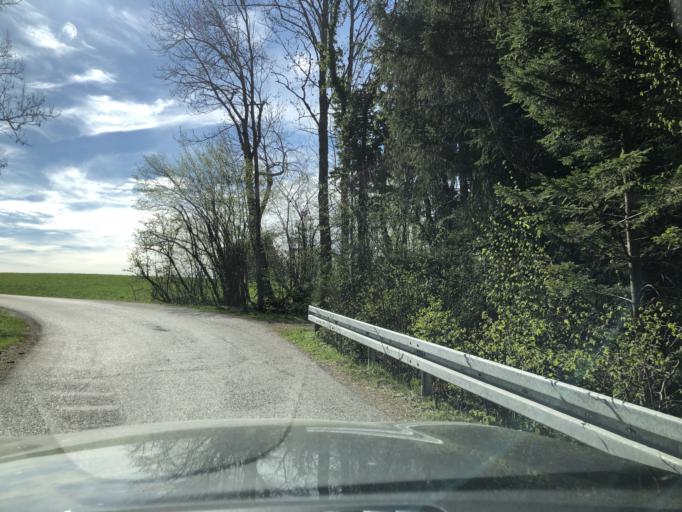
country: DE
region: Bavaria
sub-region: Swabia
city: Ruckholz
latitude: 47.6584
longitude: 10.5346
